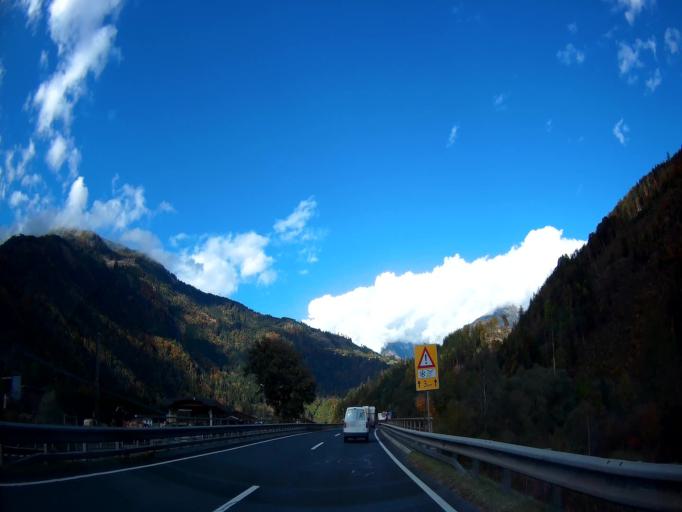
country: AT
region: Carinthia
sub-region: Politischer Bezirk Spittal an der Drau
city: Sachsenburg
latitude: 46.8163
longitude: 13.3531
